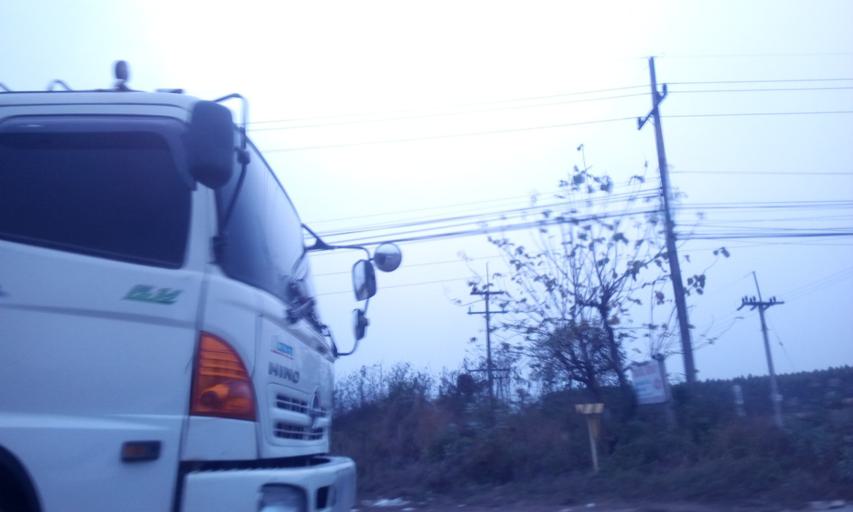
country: TH
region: Chachoengsao
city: Plaeng Yao
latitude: 13.5408
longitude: 101.2629
